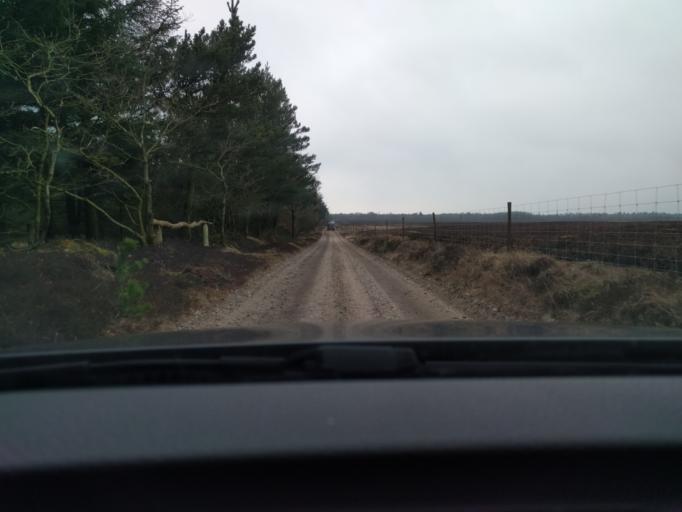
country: DK
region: Central Jutland
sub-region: Holstebro Kommune
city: Vinderup
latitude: 56.5002
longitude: 8.9212
